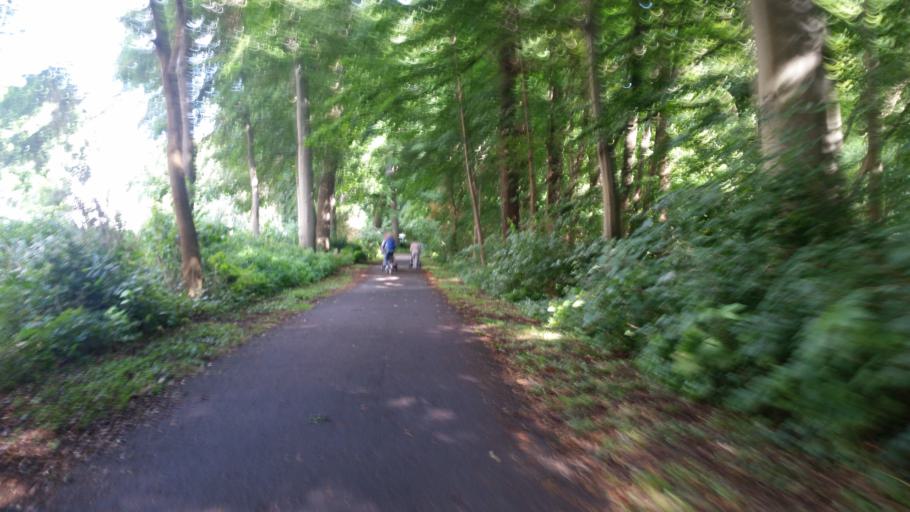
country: DE
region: Lower Saxony
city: Hannover
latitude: 52.3811
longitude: 9.7565
